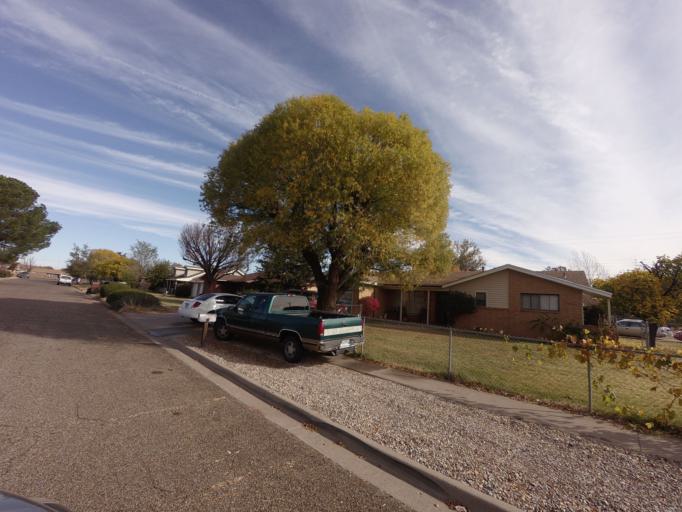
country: US
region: New Mexico
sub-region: Curry County
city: Clovis
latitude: 34.4219
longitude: -103.2265
